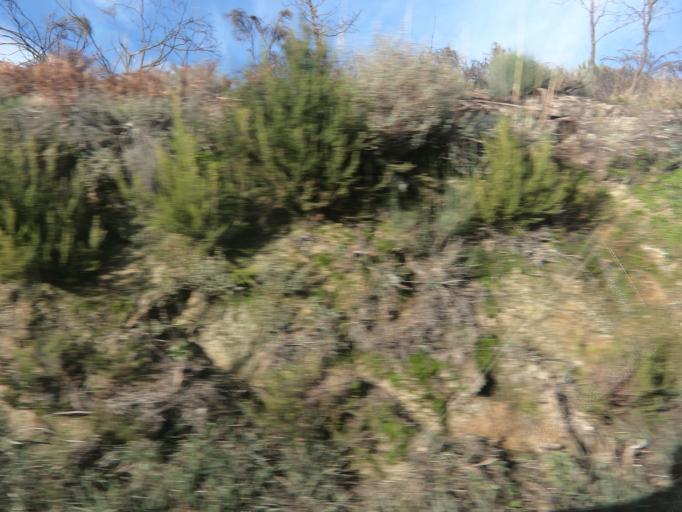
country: PT
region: Vila Real
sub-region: Sabrosa
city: Sabrosa
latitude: 41.3049
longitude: -7.6023
